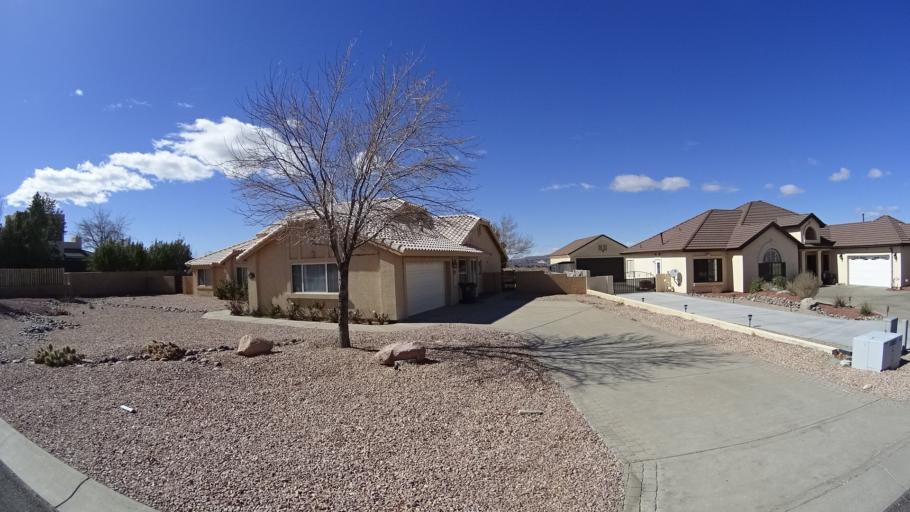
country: US
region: Arizona
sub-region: Mohave County
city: Kingman
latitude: 35.2000
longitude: -113.9753
